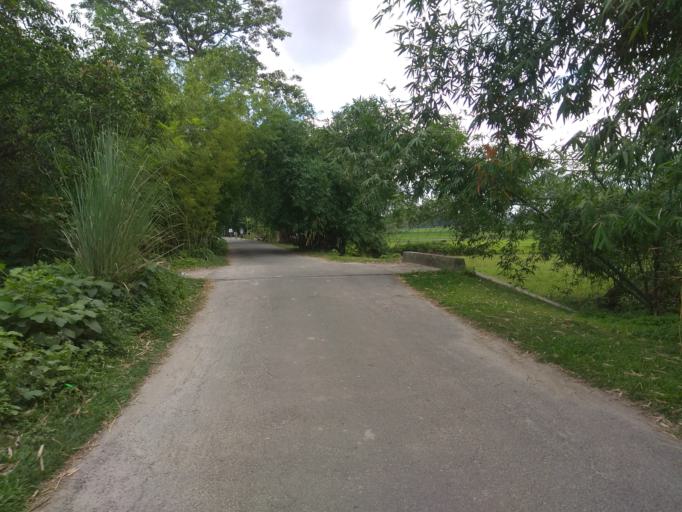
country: IN
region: West Bengal
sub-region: Koch Bihar
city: Haldibari
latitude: 26.2007
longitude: 88.9214
